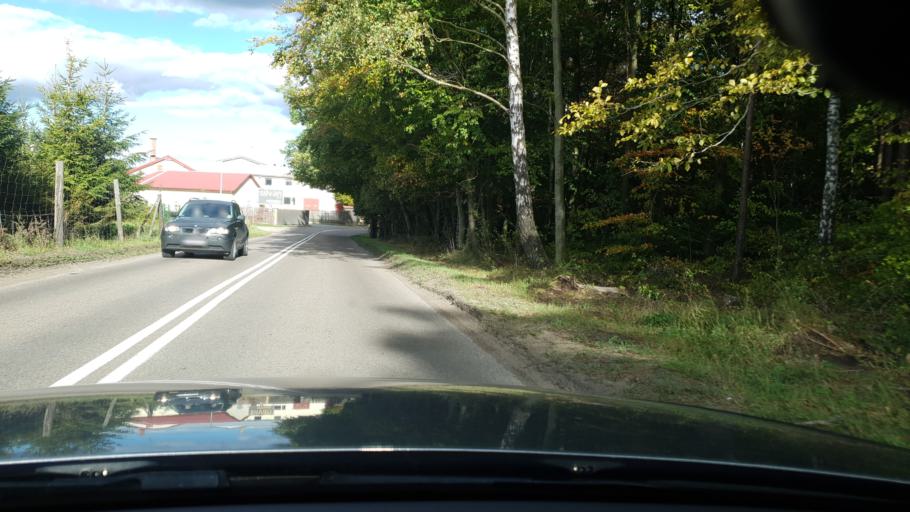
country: PL
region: Pomeranian Voivodeship
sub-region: Powiat wejherowski
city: Bojano
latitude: 54.5084
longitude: 18.3815
